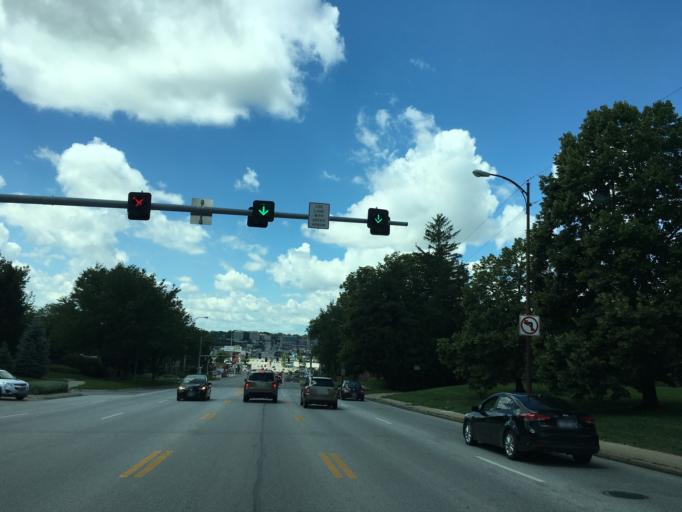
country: US
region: Nebraska
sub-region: Douglas County
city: Ralston
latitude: 41.2596
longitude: -96.0170
